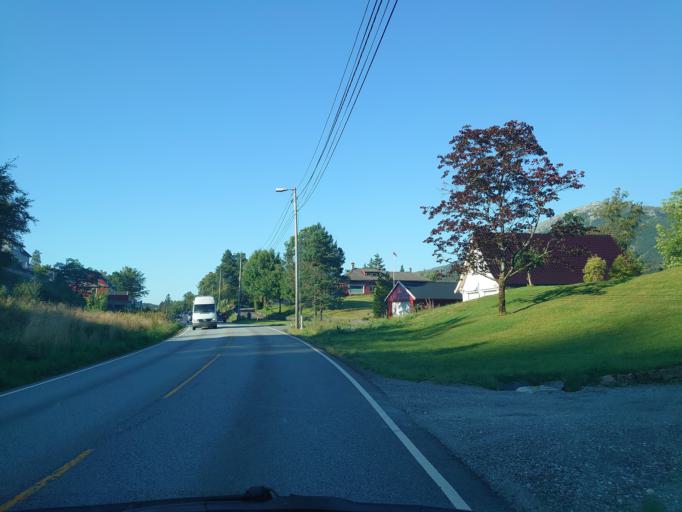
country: NO
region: Hordaland
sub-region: Bergen
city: Espeland
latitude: 60.3658
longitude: 5.4551
